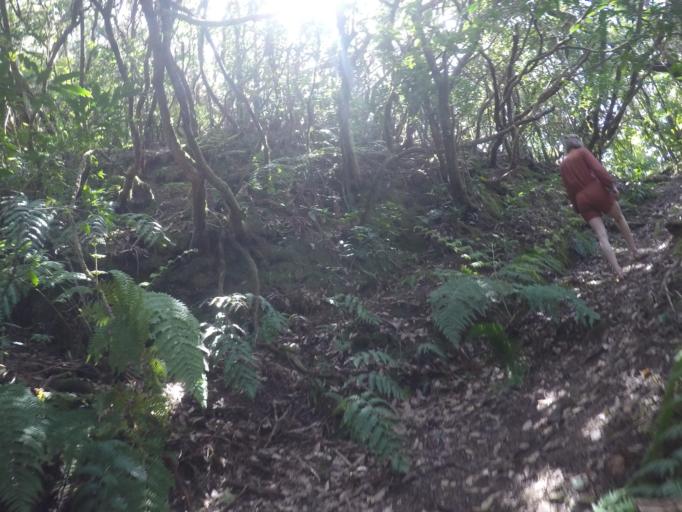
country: ES
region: Canary Islands
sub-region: Provincia de Santa Cruz de Tenerife
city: Santa Cruz de Tenerife
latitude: 28.5439
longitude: -16.2262
